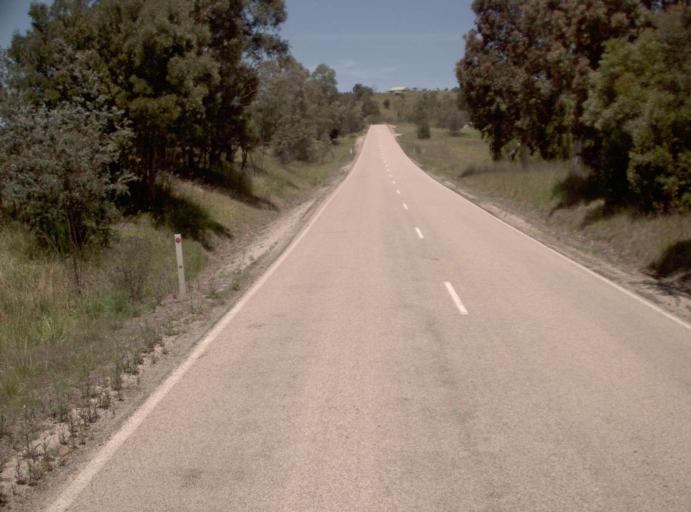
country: AU
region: Victoria
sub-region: East Gippsland
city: Bairnsdale
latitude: -37.5017
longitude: 147.8415
